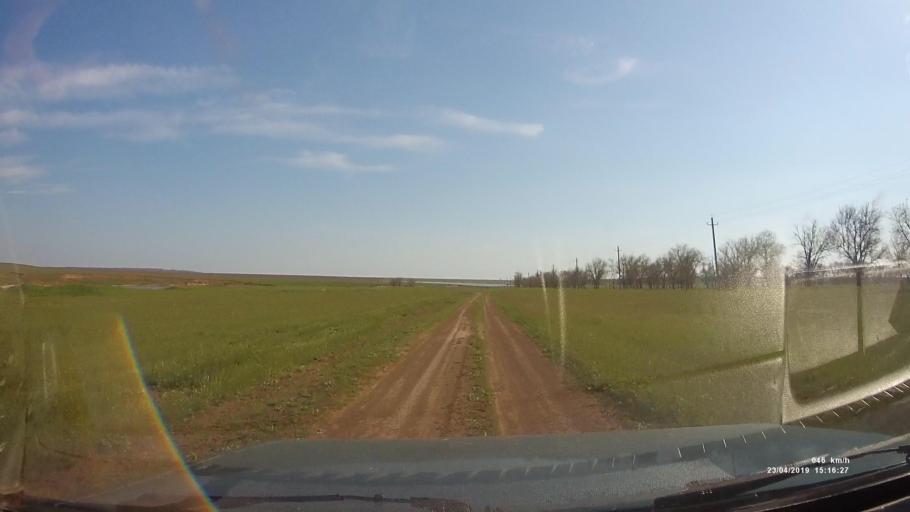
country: RU
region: Rostov
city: Remontnoye
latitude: 46.5334
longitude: 42.9699
